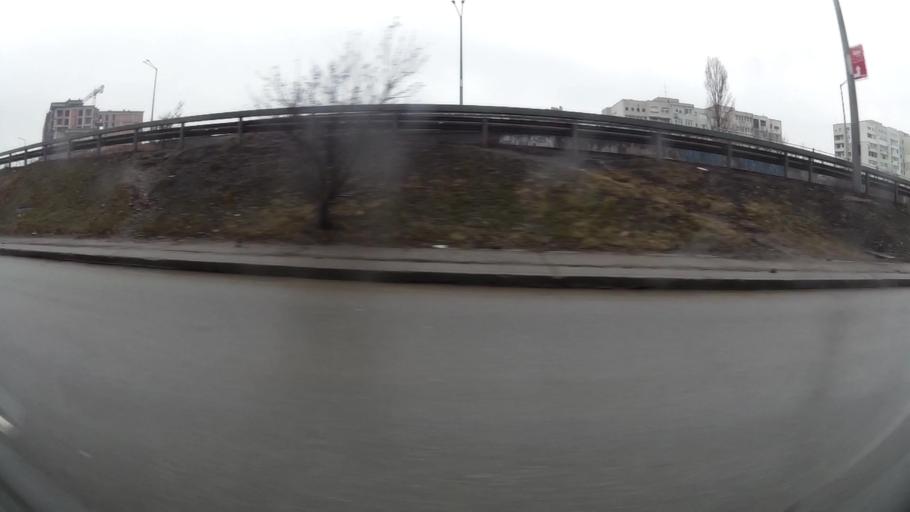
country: BG
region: Sofia-Capital
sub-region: Stolichna Obshtina
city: Sofia
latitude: 42.6274
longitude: 23.3733
